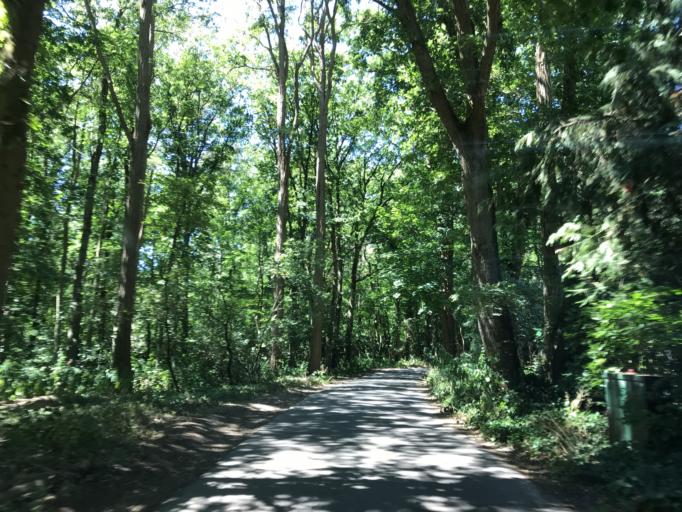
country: NL
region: North Holland
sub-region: Gemeente Huizen
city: Huizen
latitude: 52.3015
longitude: 5.2140
